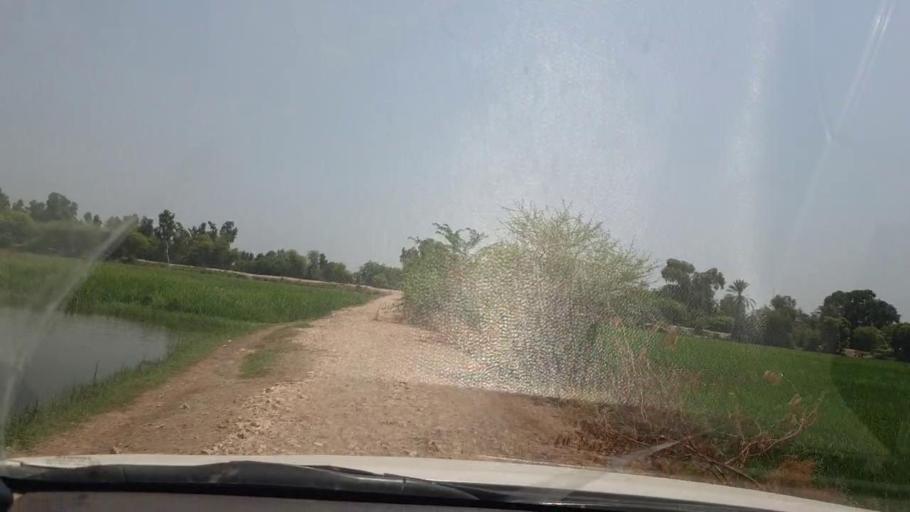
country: PK
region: Sindh
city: Lakhi
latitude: 27.9190
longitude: 68.6965
